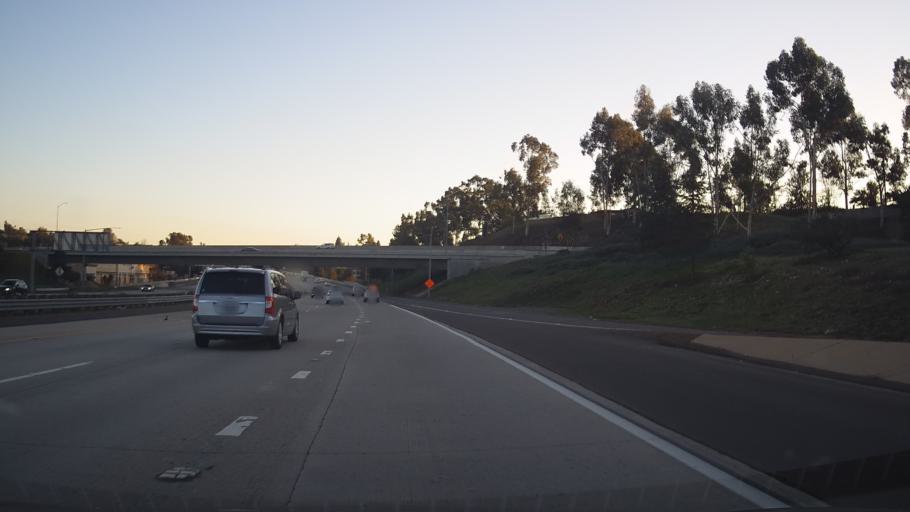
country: US
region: California
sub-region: San Diego County
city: La Mesa
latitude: 32.7885
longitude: -117.0068
